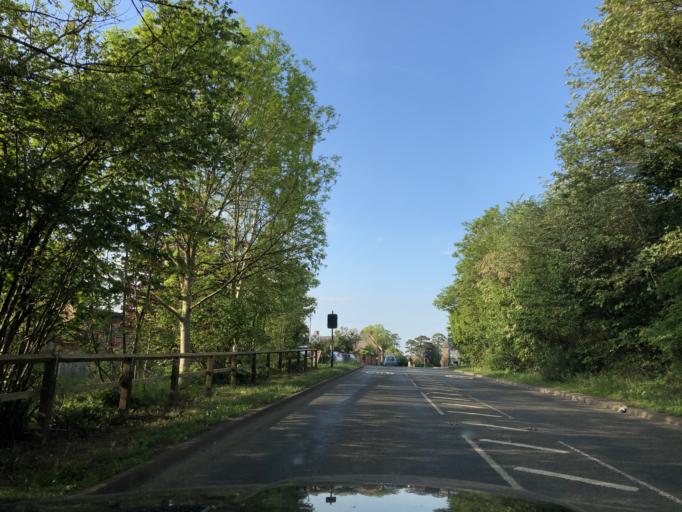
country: GB
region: England
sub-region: Warwickshire
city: Shipston on Stour
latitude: 52.1069
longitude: -1.6221
